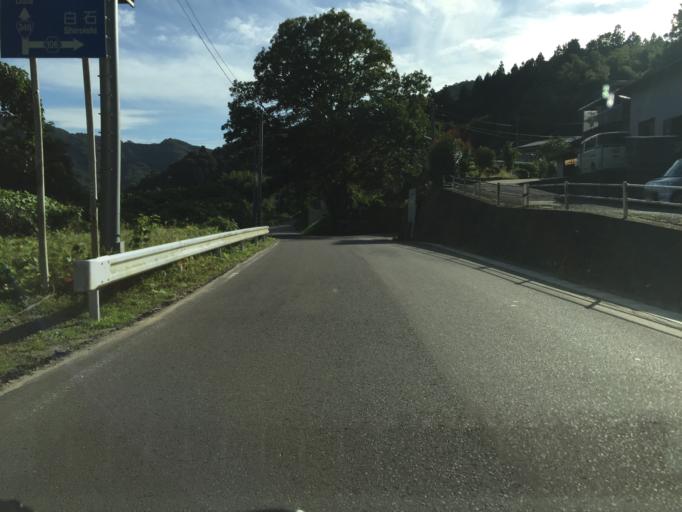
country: JP
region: Fukushima
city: Yanagawamachi-saiwaicho
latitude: 37.9112
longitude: 140.6625
